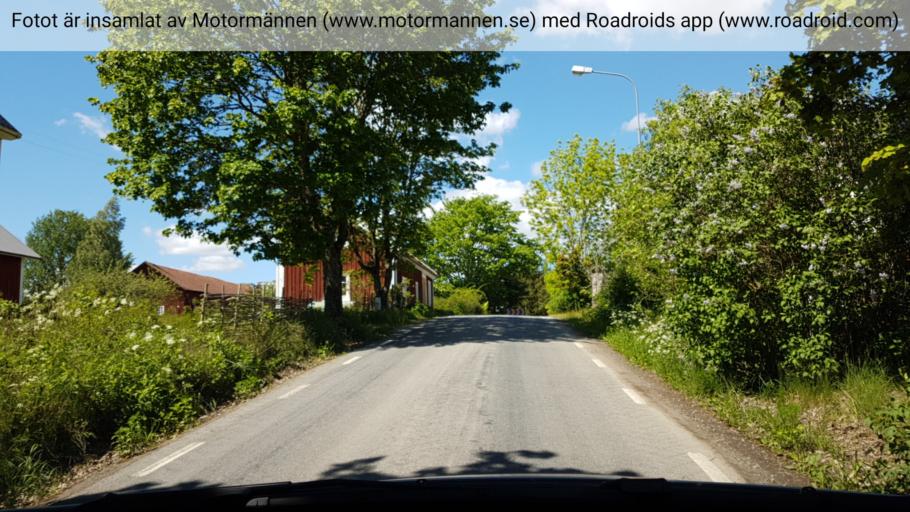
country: SE
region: Kalmar
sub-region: Vasterviks Kommun
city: Forserum
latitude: 58.0084
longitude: 16.5795
